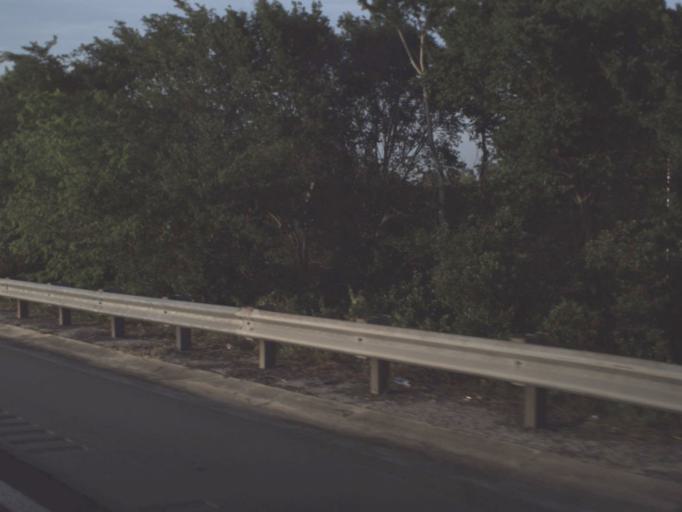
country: US
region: Florida
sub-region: Volusia County
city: Oak Hill
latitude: 28.7727
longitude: -80.8942
